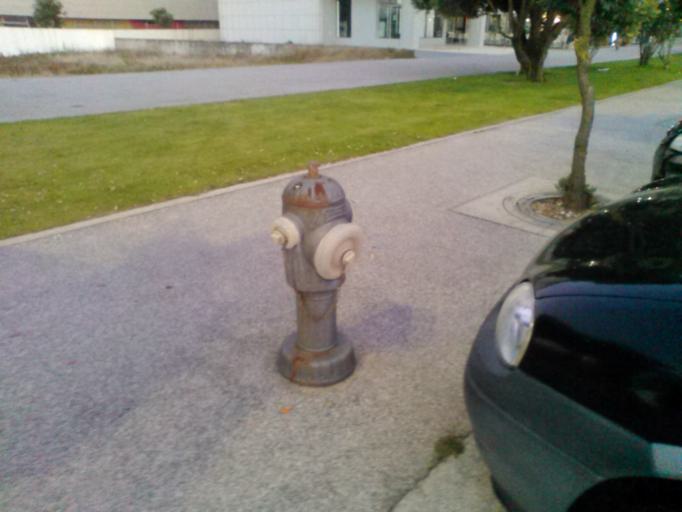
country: PT
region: Porto
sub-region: Vila do Conde
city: Vila do Conde
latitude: 41.3483
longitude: -8.7529
